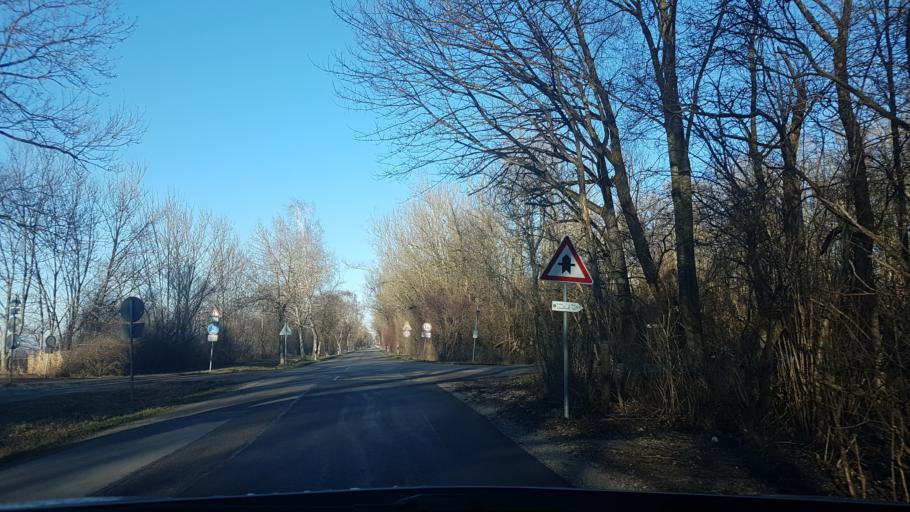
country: DE
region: Bavaria
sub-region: Upper Bavaria
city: Eichenried
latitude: 48.2811
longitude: 11.7520
